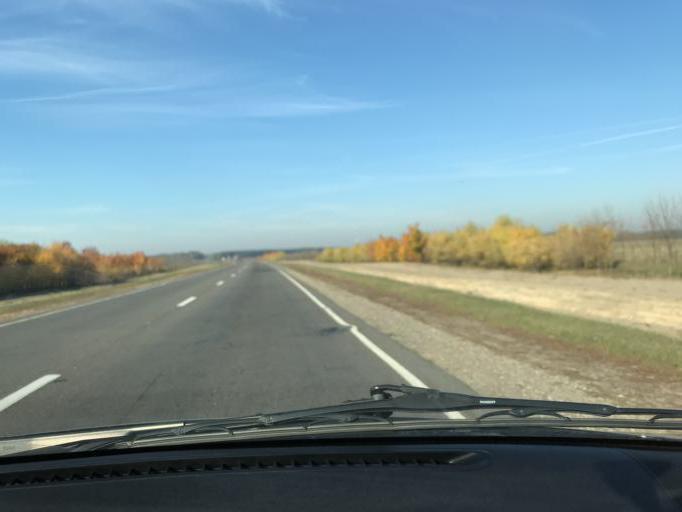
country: BY
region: Brest
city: Luninyets
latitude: 52.2741
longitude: 26.9803
